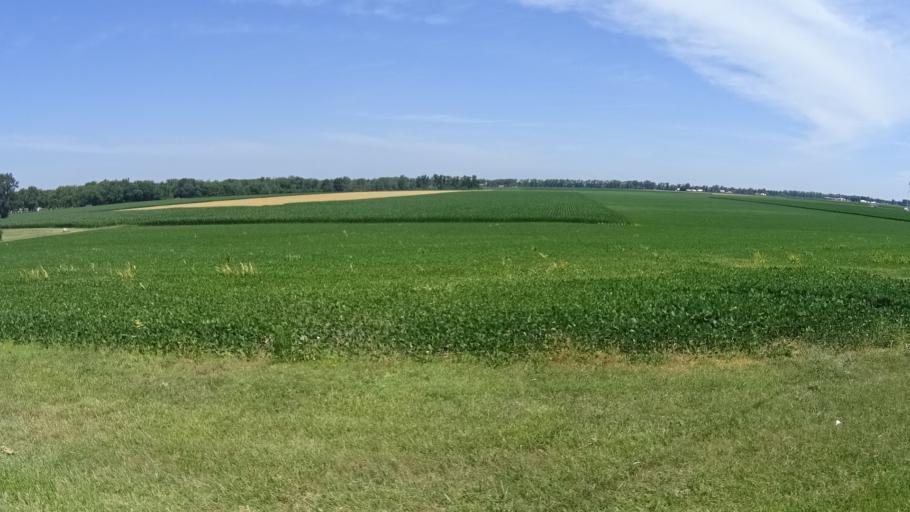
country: US
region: Ohio
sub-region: Erie County
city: Sandusky
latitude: 41.4038
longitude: -82.7950
